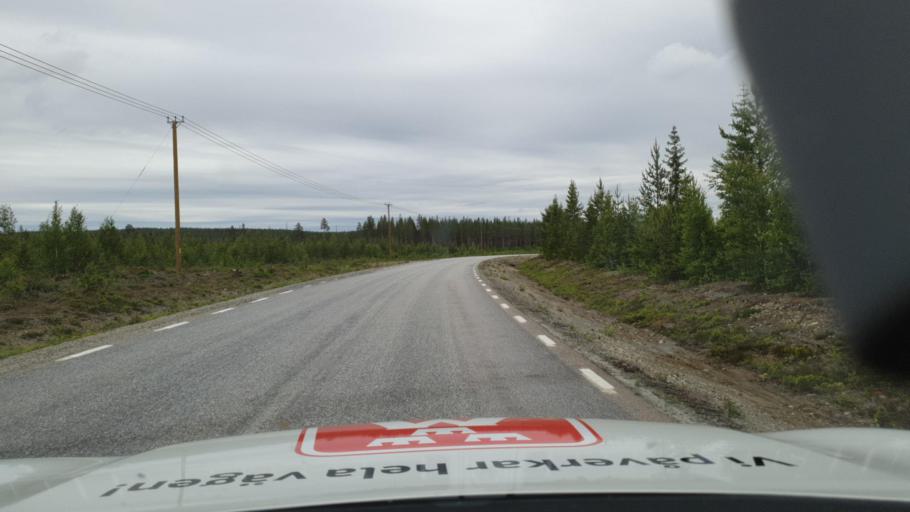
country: SE
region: Vaesterbotten
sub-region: Lycksele Kommun
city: Lycksele
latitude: 64.1165
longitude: 18.3628
